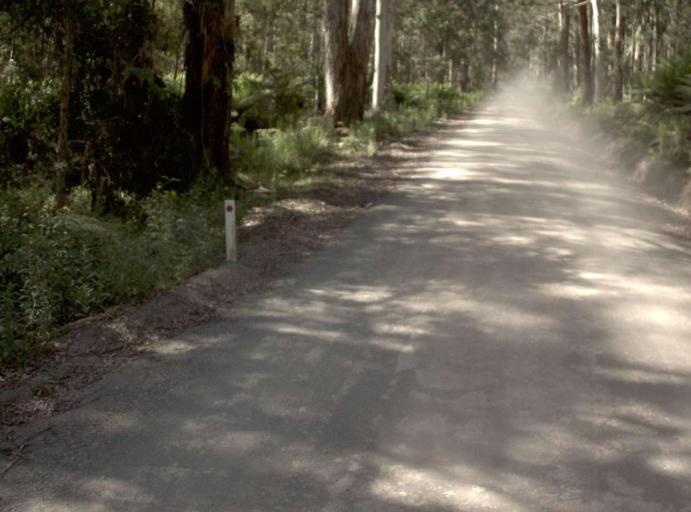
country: AU
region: New South Wales
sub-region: Bombala
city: Bombala
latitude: -37.2340
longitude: 148.7542
